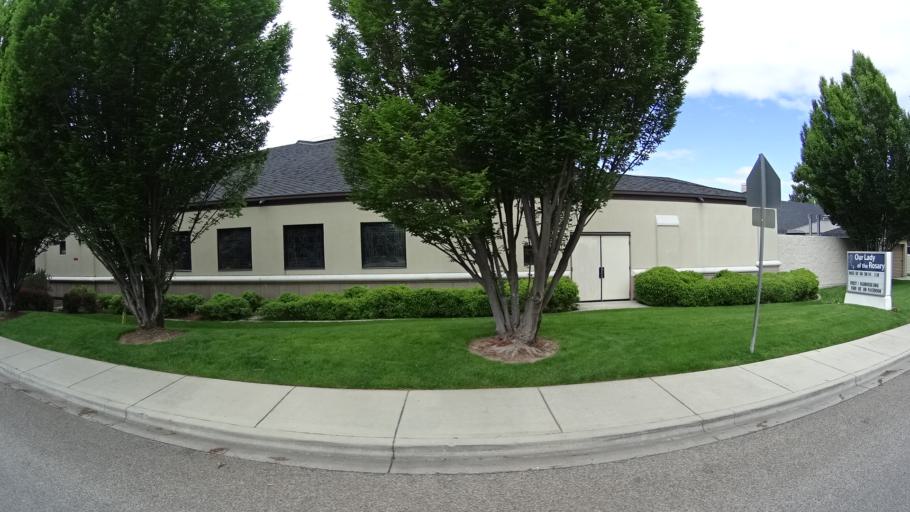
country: US
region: Idaho
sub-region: Ada County
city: Boise
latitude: 43.5719
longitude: -116.1635
